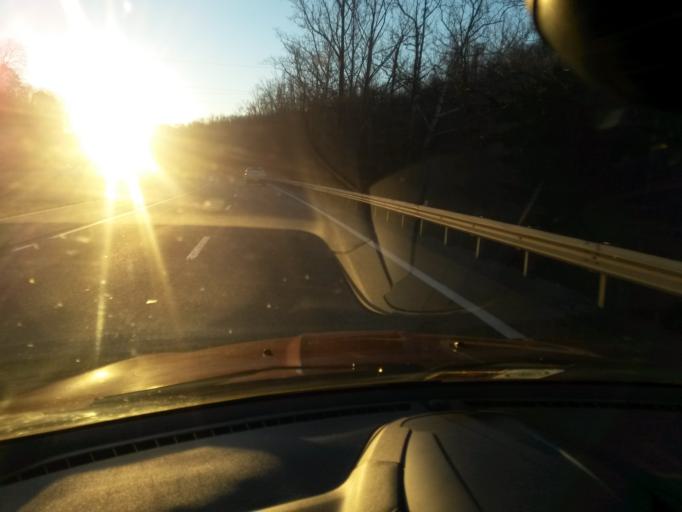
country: US
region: Virginia
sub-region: Roanoke County
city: Narrows
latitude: 37.1313
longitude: -79.9704
